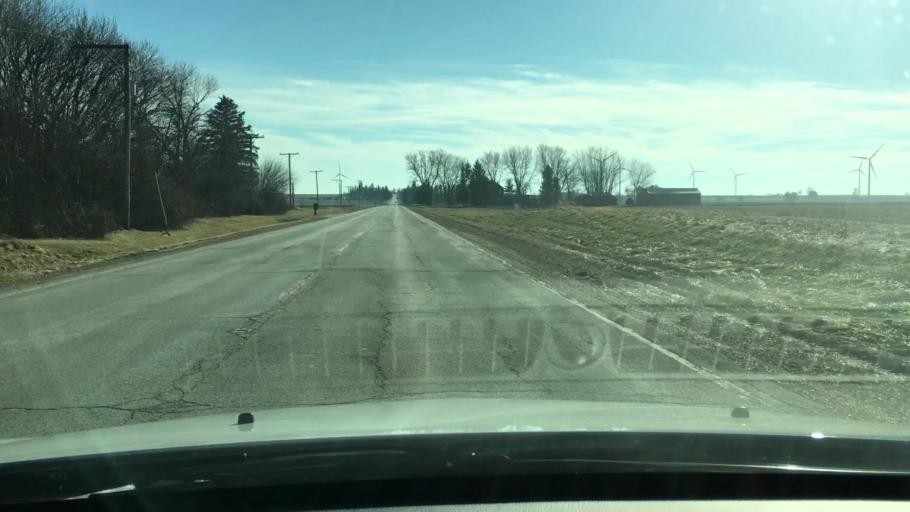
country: US
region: Illinois
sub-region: LaSalle County
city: Mendota
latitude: 41.6488
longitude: -89.1296
